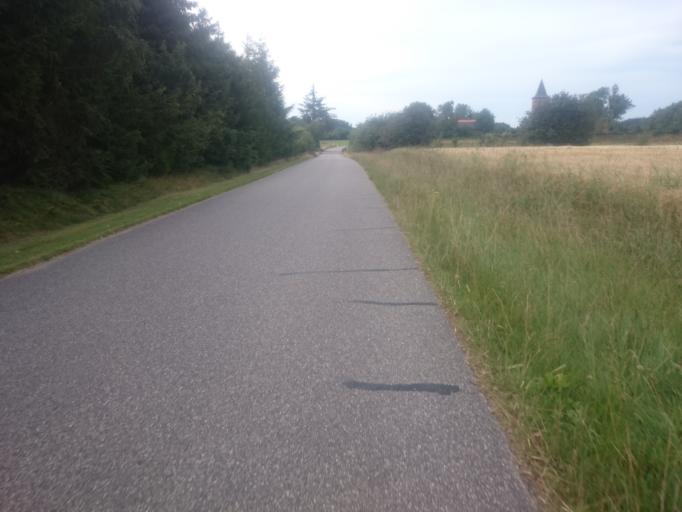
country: DK
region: South Denmark
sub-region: Billund Kommune
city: Billund
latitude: 55.7304
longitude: 9.0758
